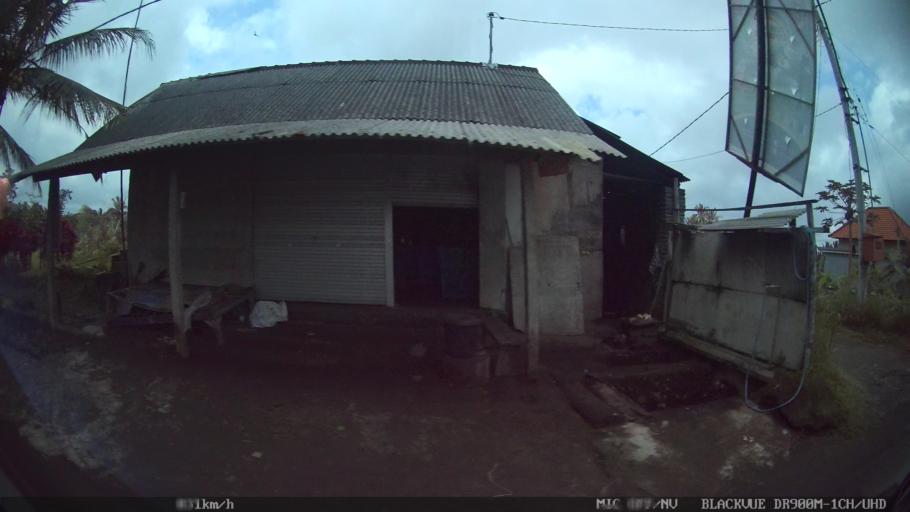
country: ID
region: Bali
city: Pemijian
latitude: -8.4373
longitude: 115.2269
